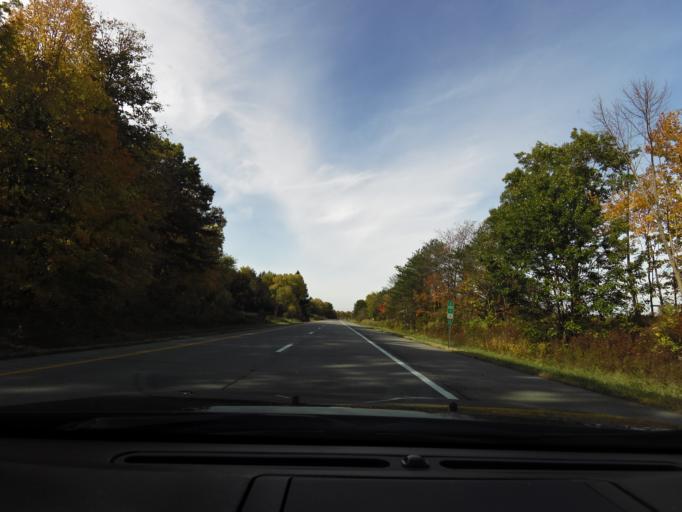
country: US
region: New York
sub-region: Erie County
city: Elma Center
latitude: 42.8150
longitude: -78.6549
